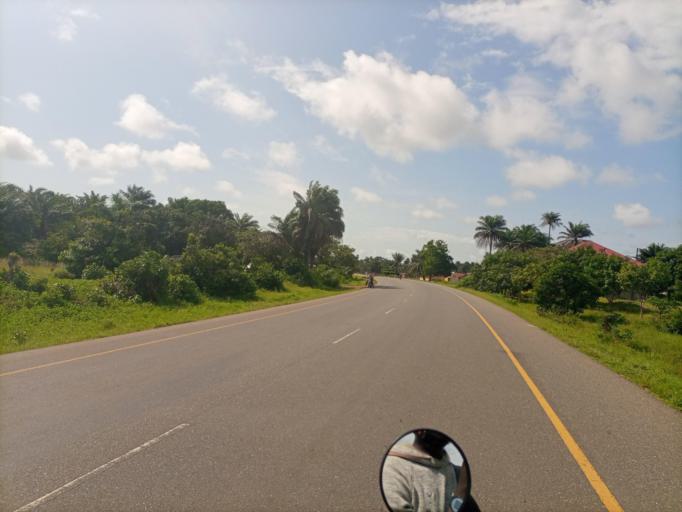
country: SL
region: Northern Province
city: Masoyila
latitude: 8.6164
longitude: -13.1746
